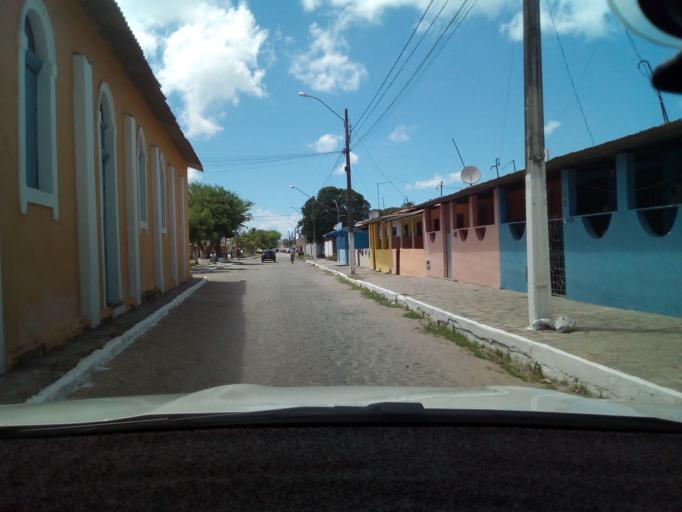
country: BR
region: Paraiba
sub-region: Cabedelo
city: Cabedelo
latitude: -6.9814
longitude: -34.8342
